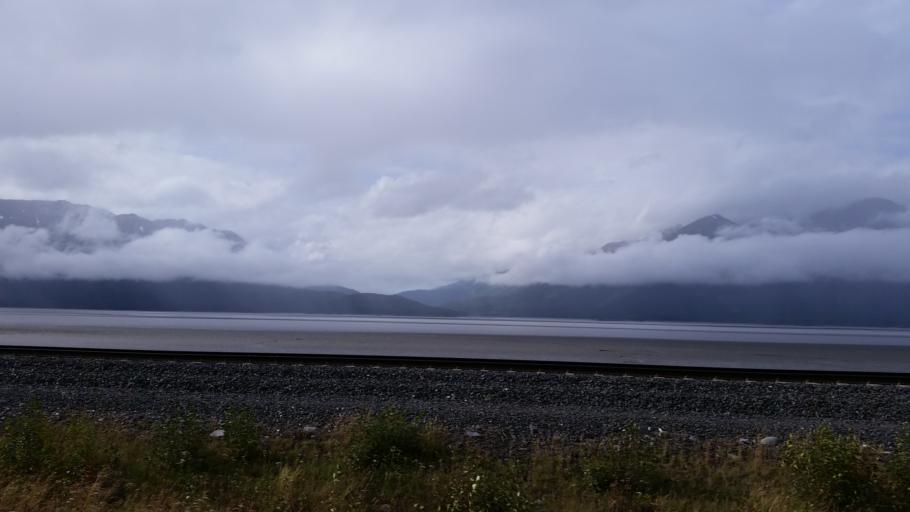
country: US
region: Alaska
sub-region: Anchorage Municipality
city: Girdwood
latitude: 60.9503
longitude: -149.3991
